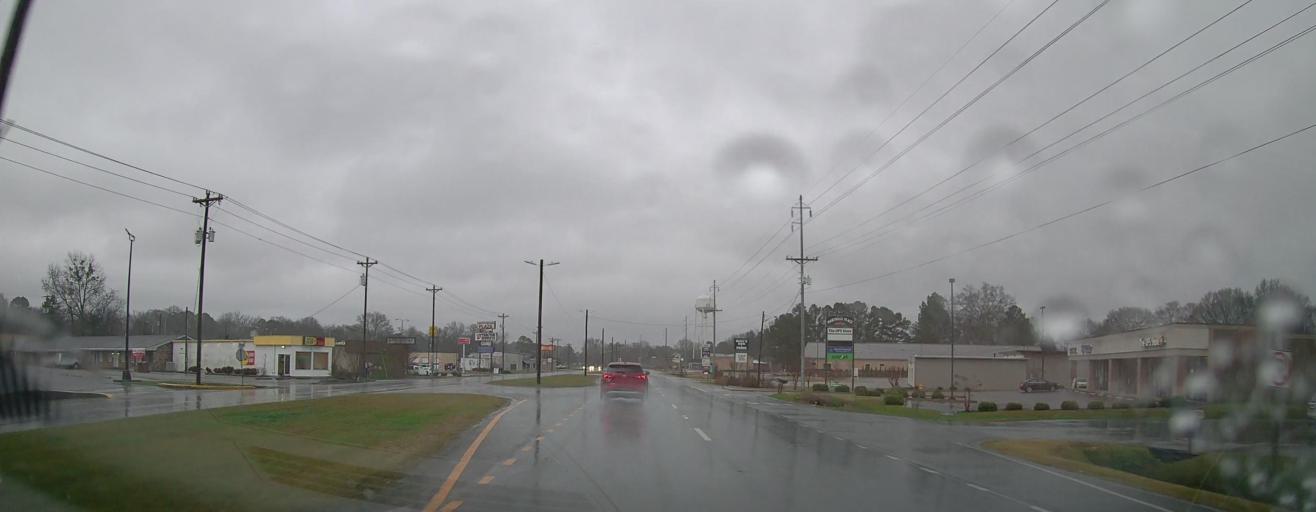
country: US
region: Alabama
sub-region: Morgan County
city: Hartselle
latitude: 34.4392
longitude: -86.9410
